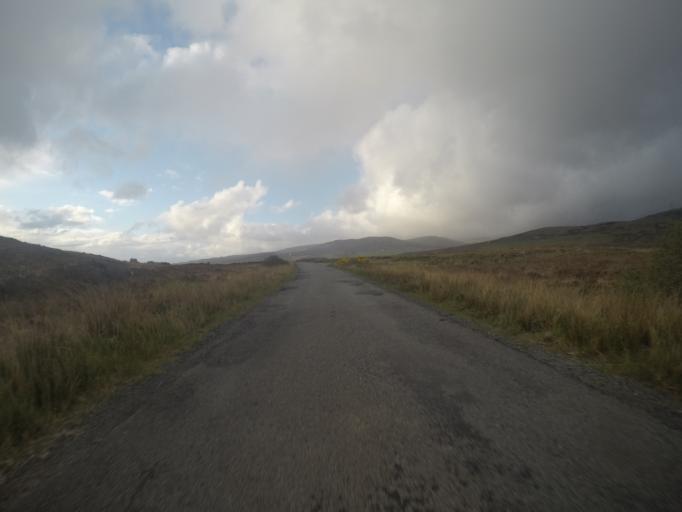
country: GB
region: Scotland
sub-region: Highland
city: Isle of Skye
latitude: 57.4608
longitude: -6.2965
